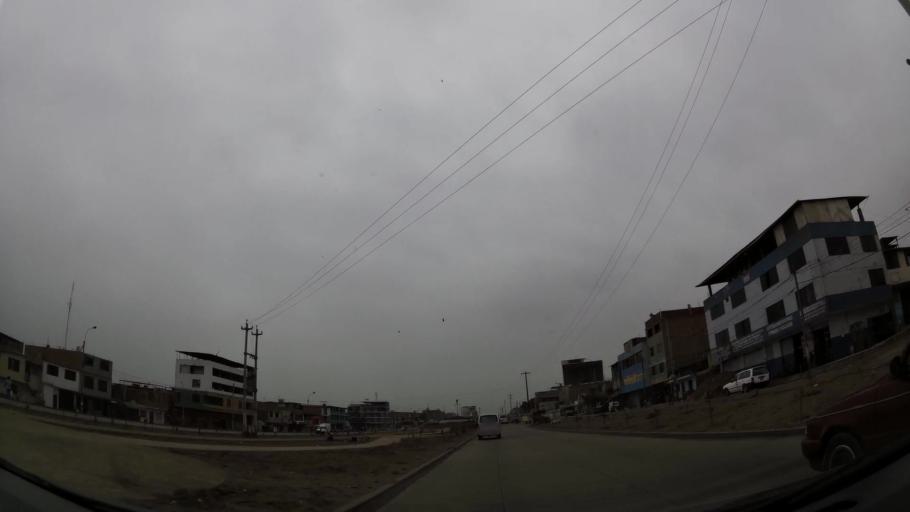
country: PE
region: Lima
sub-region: Lima
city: Surco
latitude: -12.2146
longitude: -76.9475
